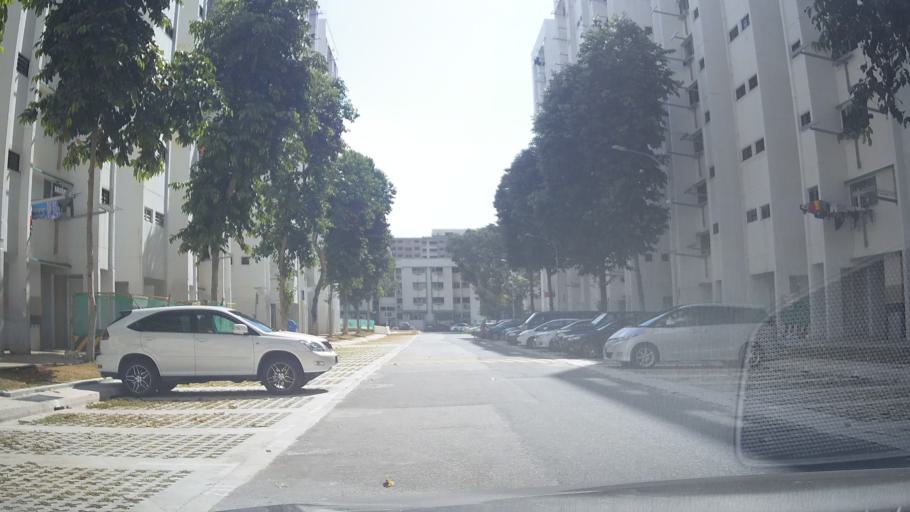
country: SG
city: Singapore
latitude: 1.3558
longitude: 103.9477
